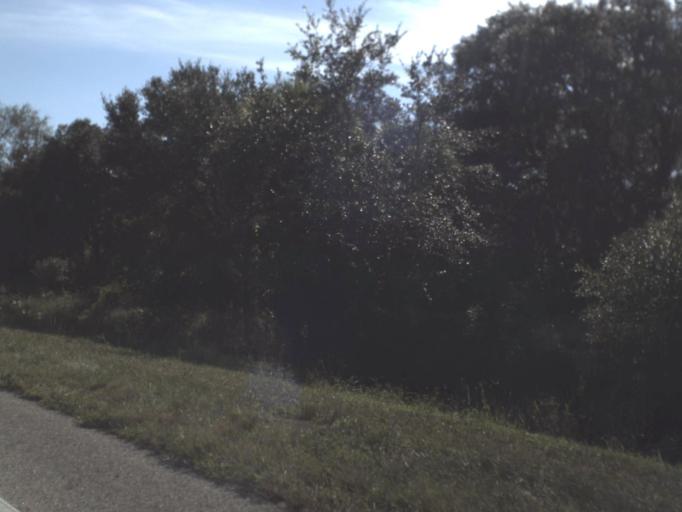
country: US
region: Florida
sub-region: Glades County
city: Moore Haven
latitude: 26.8949
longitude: -81.2382
